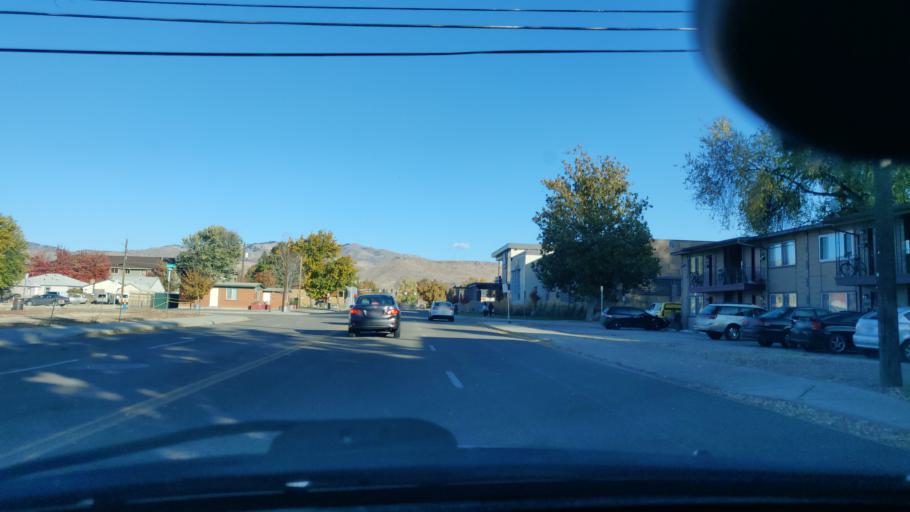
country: US
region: Idaho
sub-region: Ada County
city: Boise
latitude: 43.5984
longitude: -116.1969
